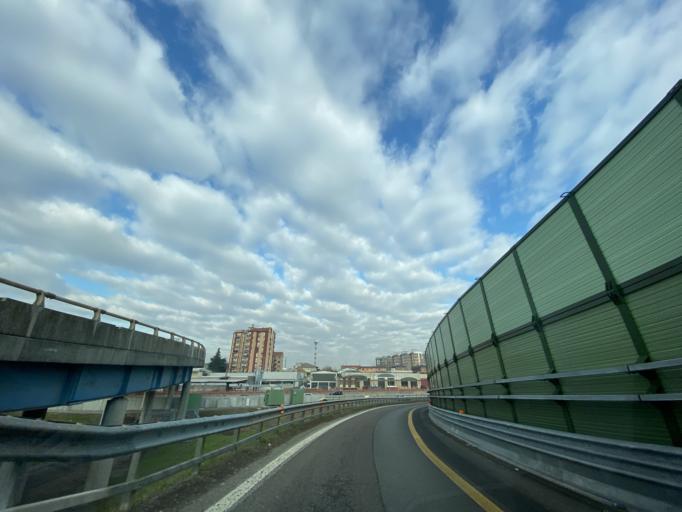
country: IT
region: Lombardy
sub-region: Citta metropolitana di Milano
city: Cormano
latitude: 45.5364
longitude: 9.1652
